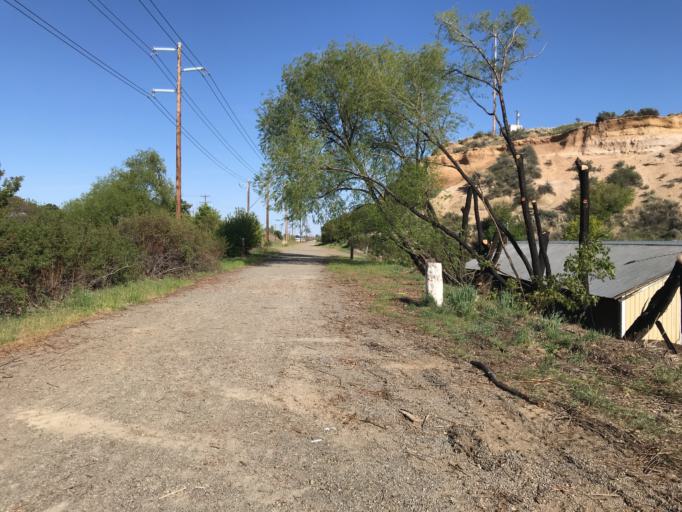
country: US
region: Washington
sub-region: Kittitas County
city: Ellensburg
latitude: 47.0007
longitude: -120.5306
